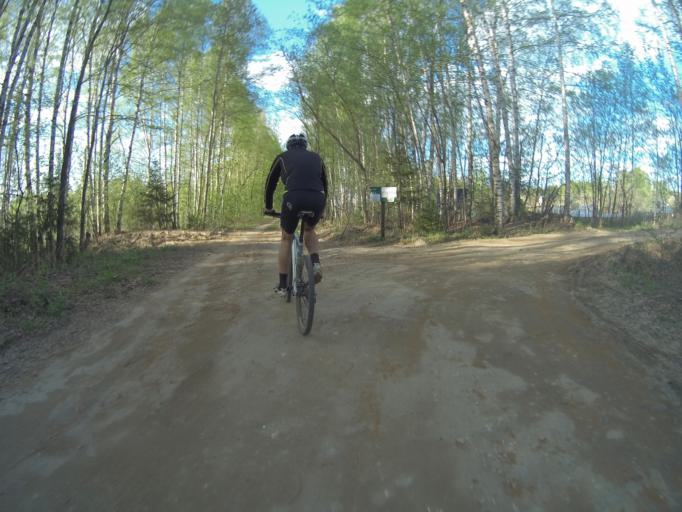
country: RU
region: Vladimir
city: Raduzhnyy
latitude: 56.0098
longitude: 40.2570
